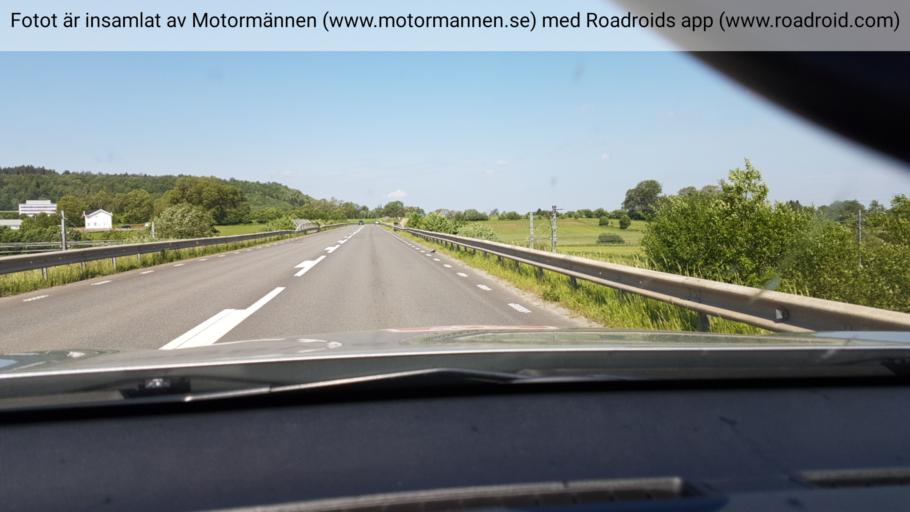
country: SE
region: Vaestra Goetaland
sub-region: Falkopings Kommun
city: Falkoeping
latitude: 58.1858
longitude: 13.5673
